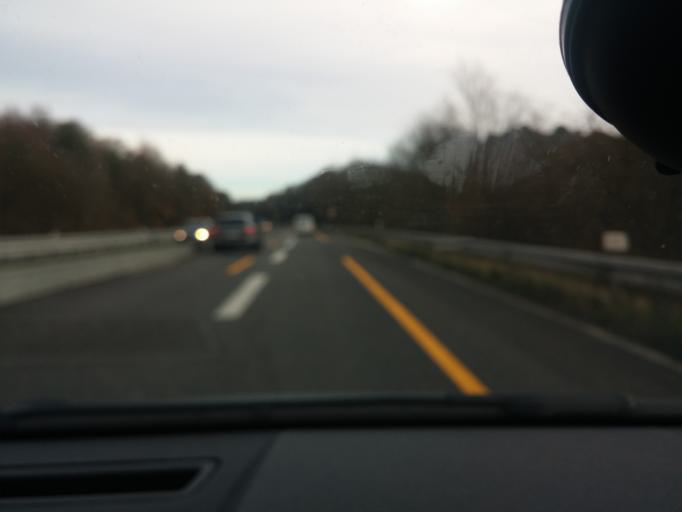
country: DE
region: Hesse
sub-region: Regierungsbezirk Darmstadt
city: Eppertshausen
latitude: 49.9572
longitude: 8.8428
